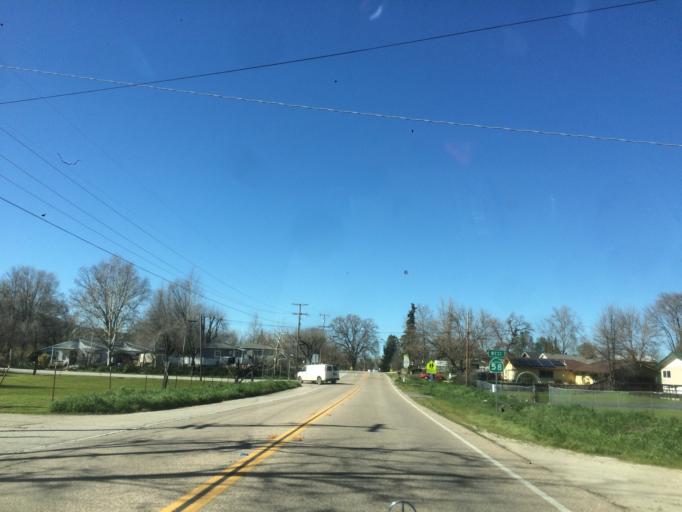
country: US
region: California
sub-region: San Luis Obispo County
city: Santa Margarita
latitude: 35.3909
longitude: -120.6026
